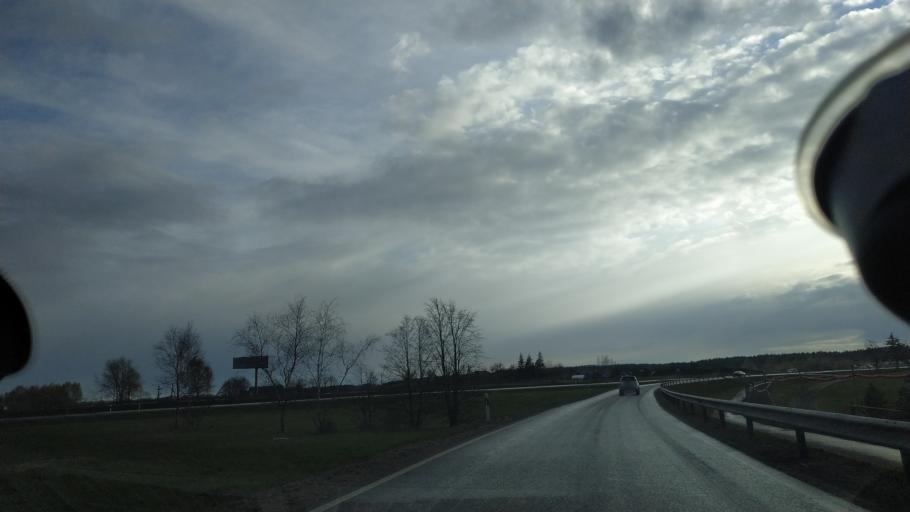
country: LT
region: Panevezys
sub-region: Panevezys City
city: Panevezys
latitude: 55.7348
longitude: 24.2730
